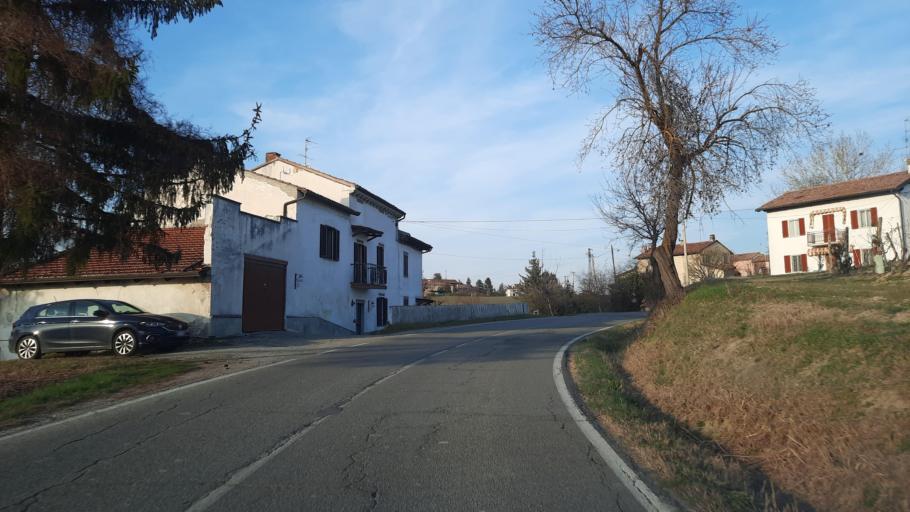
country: IT
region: Piedmont
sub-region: Provincia di Alessandria
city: Rosignano Monferrato
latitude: 45.0808
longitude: 8.4111
